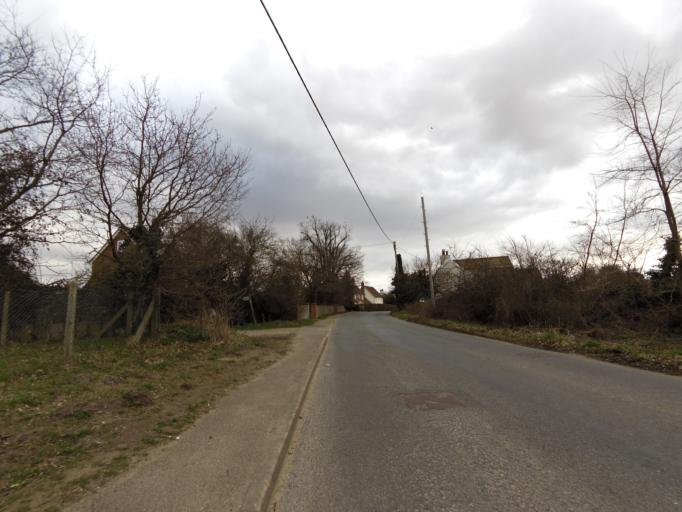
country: GB
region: England
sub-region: Suffolk
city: Felixstowe
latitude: 52.0128
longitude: 1.3149
